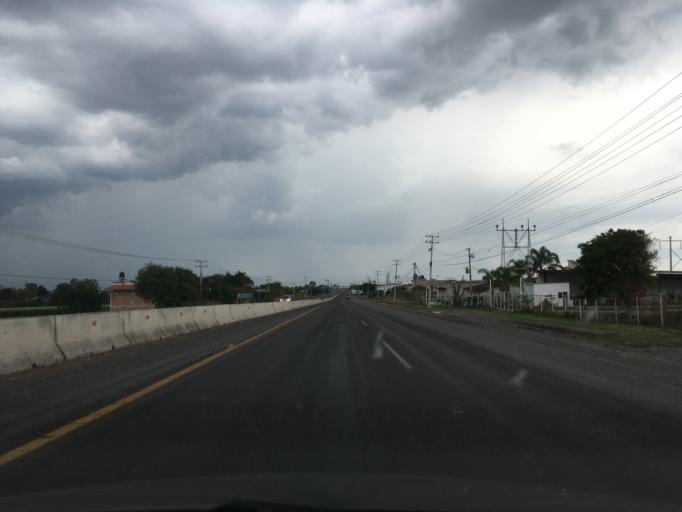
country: MX
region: Guanajuato
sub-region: Celaya
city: El Sauz (El Sauz de Villasenor)
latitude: 20.3847
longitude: -100.7929
